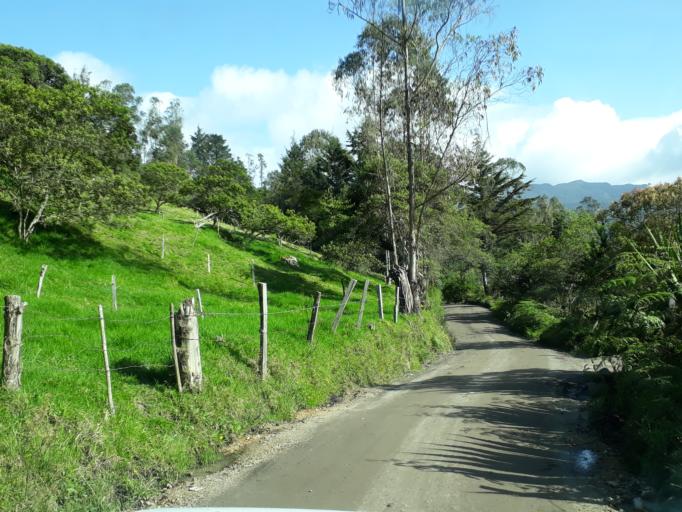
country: CO
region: Cundinamarca
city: Junin
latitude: 4.7914
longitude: -73.6778
